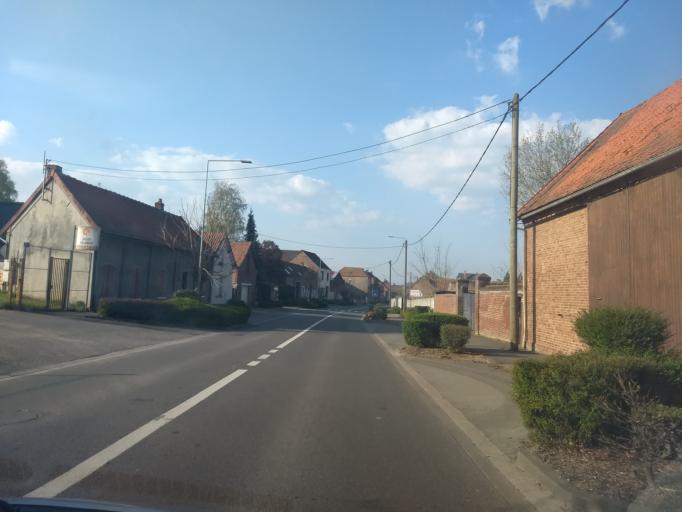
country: FR
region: Nord-Pas-de-Calais
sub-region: Departement du Pas-de-Calais
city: Bucquoy
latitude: 50.1441
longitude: 2.7123
